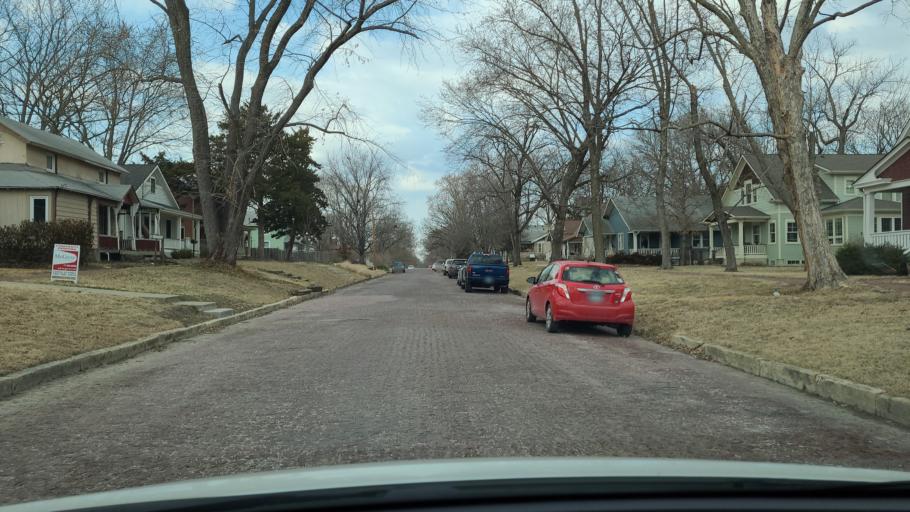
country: US
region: Kansas
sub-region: Douglas County
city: Lawrence
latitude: 38.9603
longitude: -95.2312
